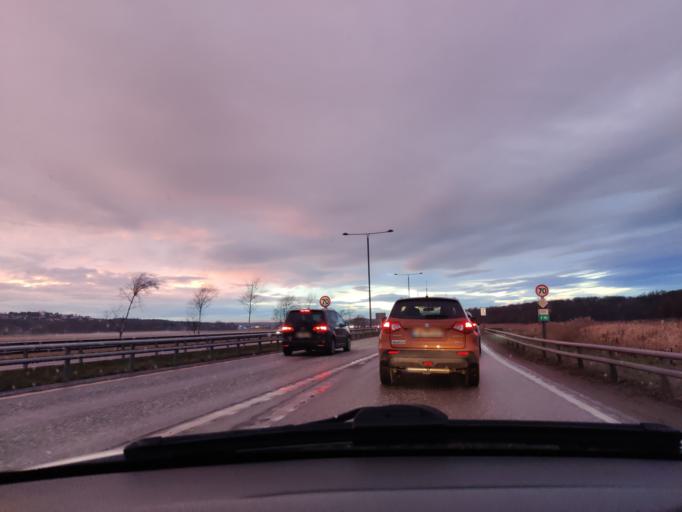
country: NO
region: Vestfold
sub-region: Tonsberg
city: Tonsberg
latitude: 59.2815
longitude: 10.3934
